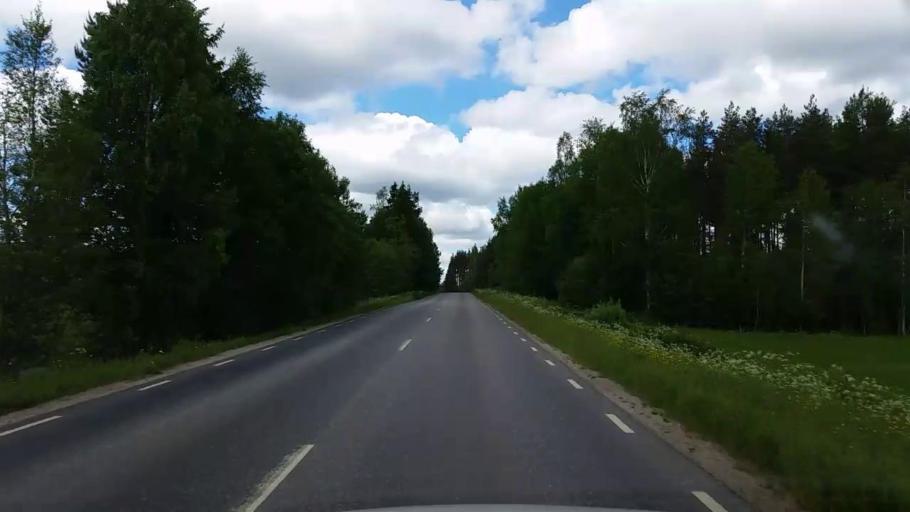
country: SE
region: Gaevleborg
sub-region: Ovanakers Kommun
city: Alfta
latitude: 61.3796
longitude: 16.0503
